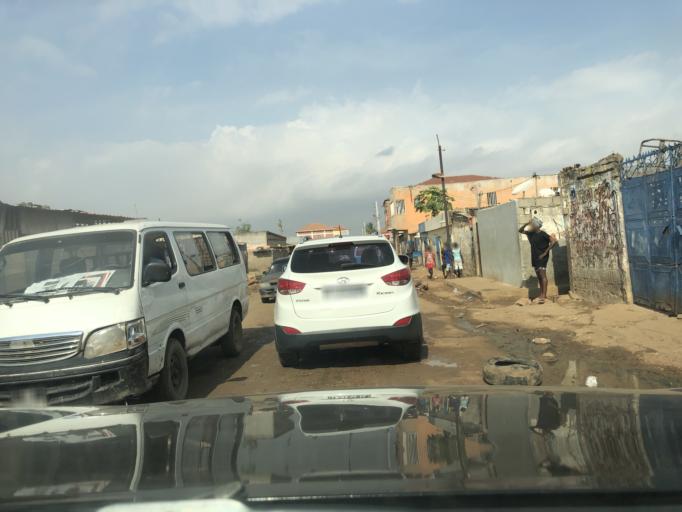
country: AO
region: Luanda
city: Luanda
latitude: -8.8571
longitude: 13.2559
